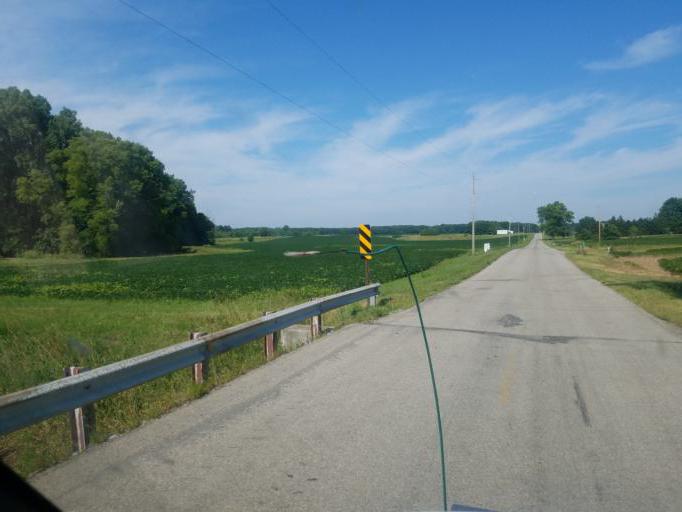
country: US
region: Ohio
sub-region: Hardin County
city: Kenton
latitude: 40.5545
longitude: -83.6460
